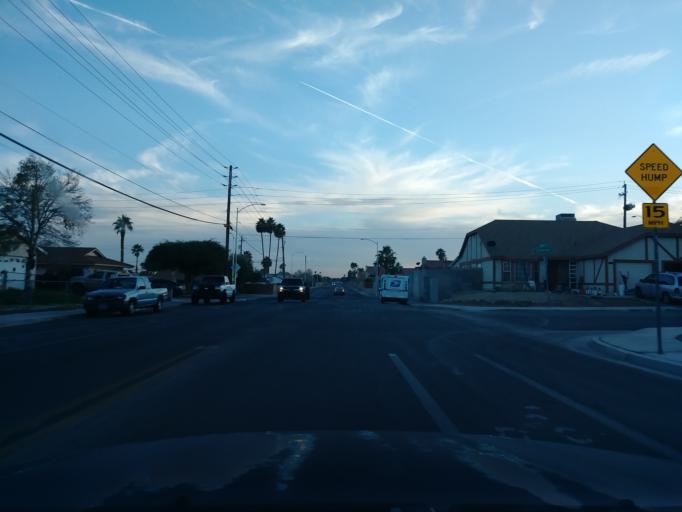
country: US
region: Nevada
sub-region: Clark County
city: Spring Valley
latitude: 36.1671
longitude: -115.2421
